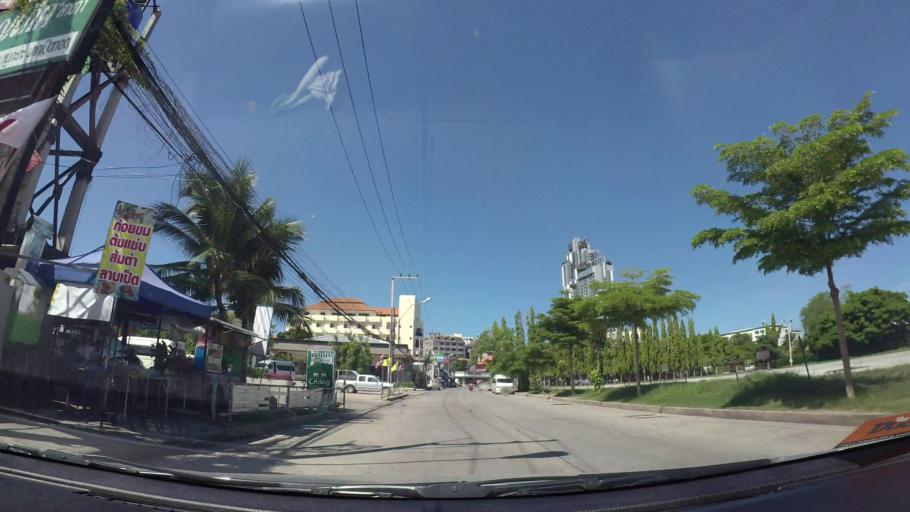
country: TH
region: Chon Buri
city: Phatthaya
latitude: 12.9422
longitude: 100.8912
